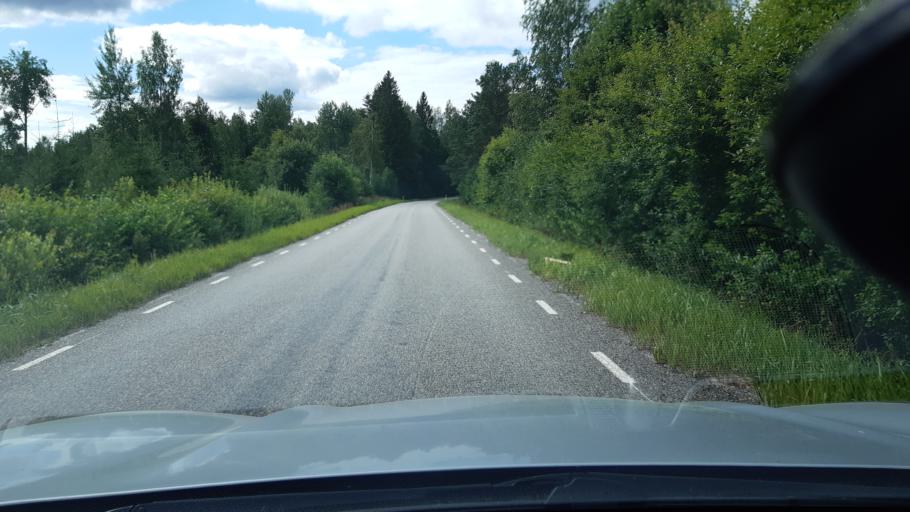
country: EE
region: Raplamaa
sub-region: Jaervakandi vald
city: Jarvakandi
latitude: 58.7946
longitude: 24.8610
